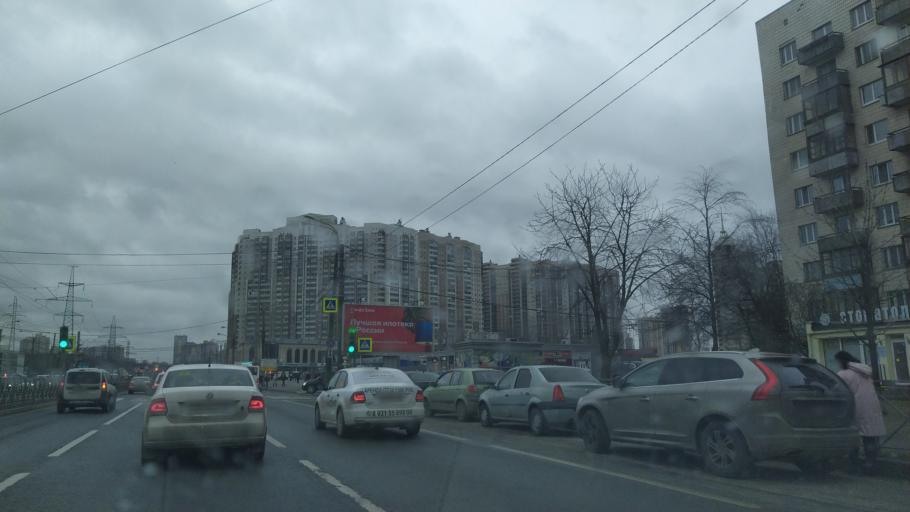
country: RU
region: St.-Petersburg
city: Novaya Derevnya
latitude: 60.0035
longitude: 30.2936
